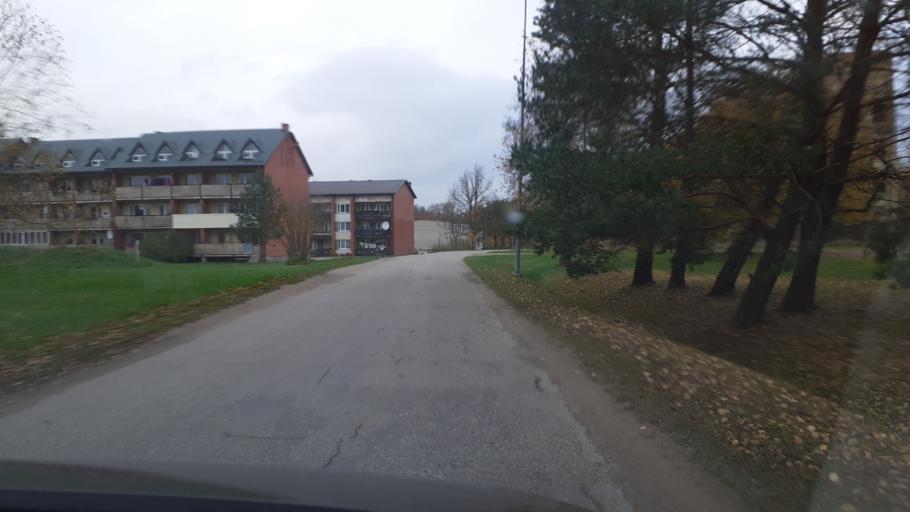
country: LV
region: Kuldigas Rajons
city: Kuldiga
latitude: 56.9836
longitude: 22.0197
